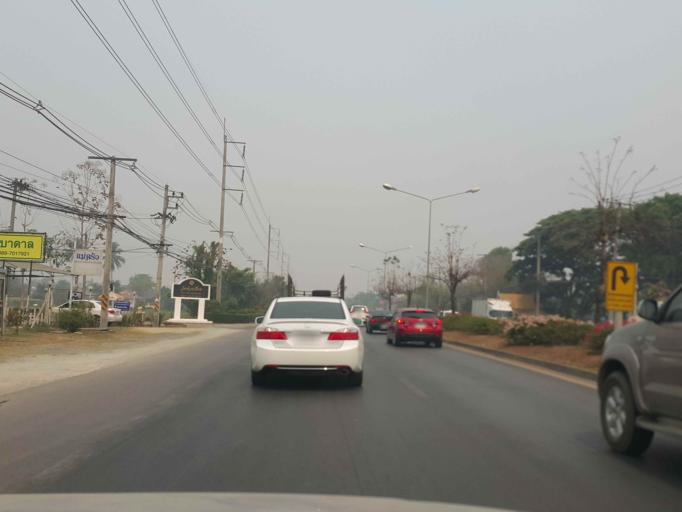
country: TH
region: Chiang Mai
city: San Sai
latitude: 18.9122
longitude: 98.9996
